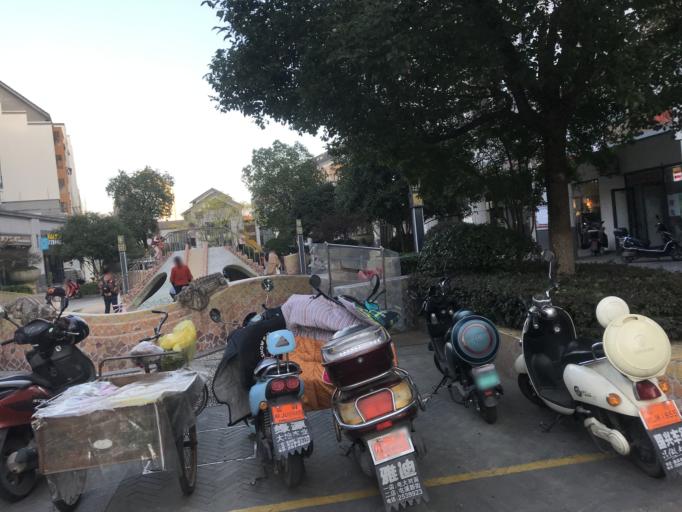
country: CN
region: Anhui Sheng
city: Liyang
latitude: 29.7093
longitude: 118.2896
